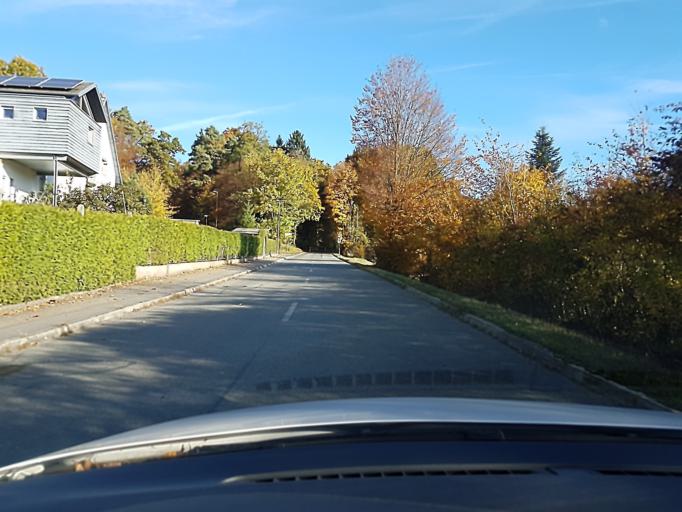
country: DE
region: Baden-Wuerttemberg
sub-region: Karlsruhe Region
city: Mosbach
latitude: 49.3901
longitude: 9.1893
